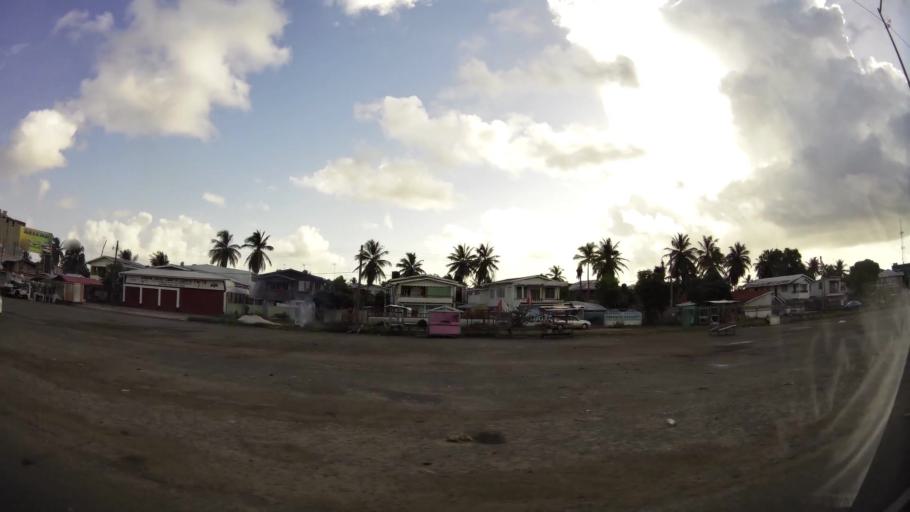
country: GY
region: Demerara-Mahaica
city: Georgetown
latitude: 6.7986
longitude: -58.0391
